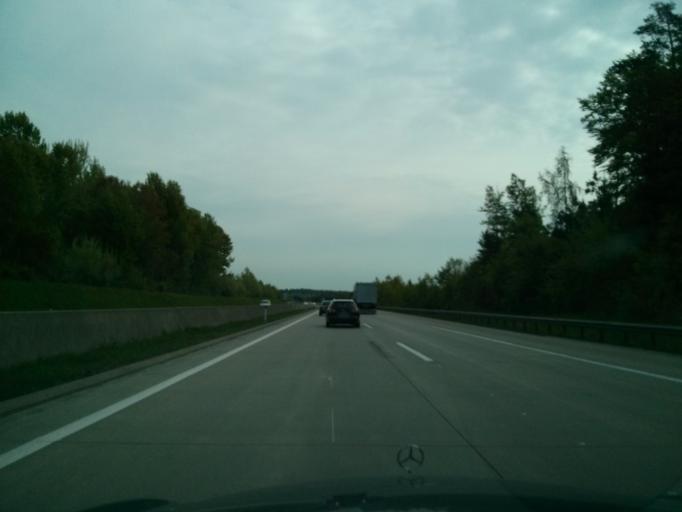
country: AT
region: Styria
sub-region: Politischer Bezirk Weiz
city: Nitscha
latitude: 47.1006
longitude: 15.7554
